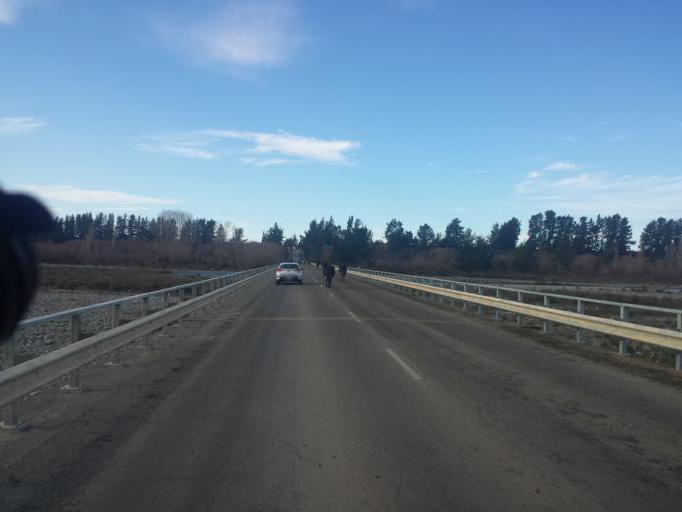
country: NZ
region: Canterbury
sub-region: Timaru District
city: Pleasant Point
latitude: -43.9744
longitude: 171.3003
